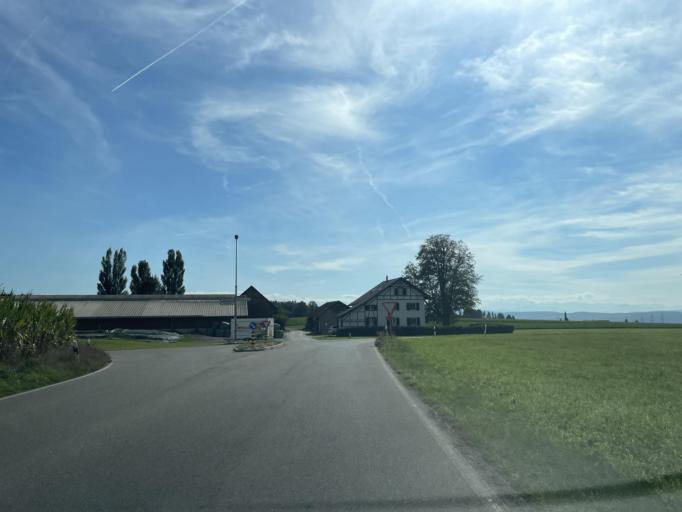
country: CH
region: Zurich
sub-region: Bezirk Winterthur
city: Brutten
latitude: 47.4651
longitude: 8.6679
